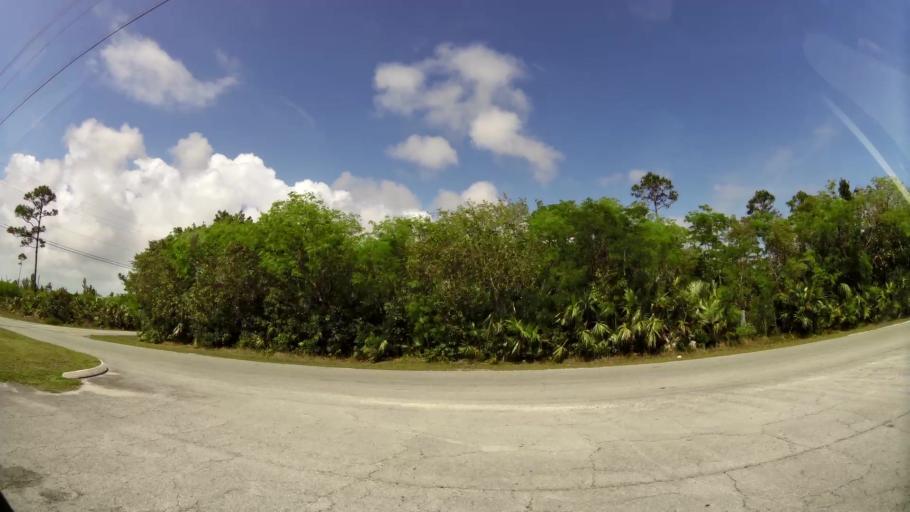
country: BS
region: Freeport
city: Freeport
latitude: 26.5023
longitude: -78.7016
